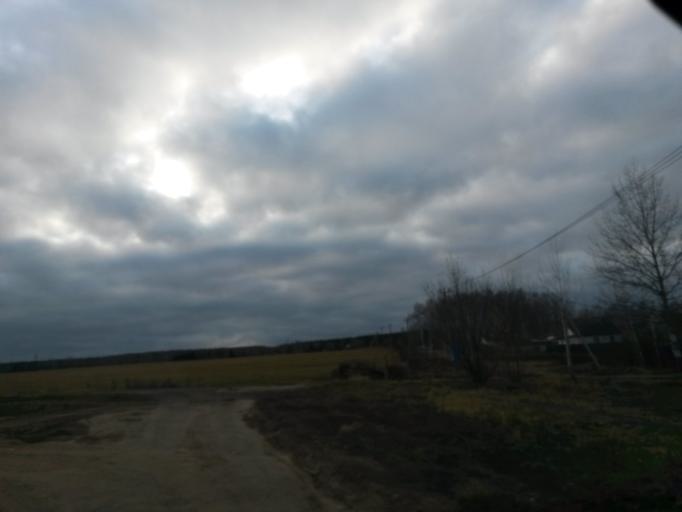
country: RU
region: Moskovskaya
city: Lyubuchany
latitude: 55.2546
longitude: 37.5935
